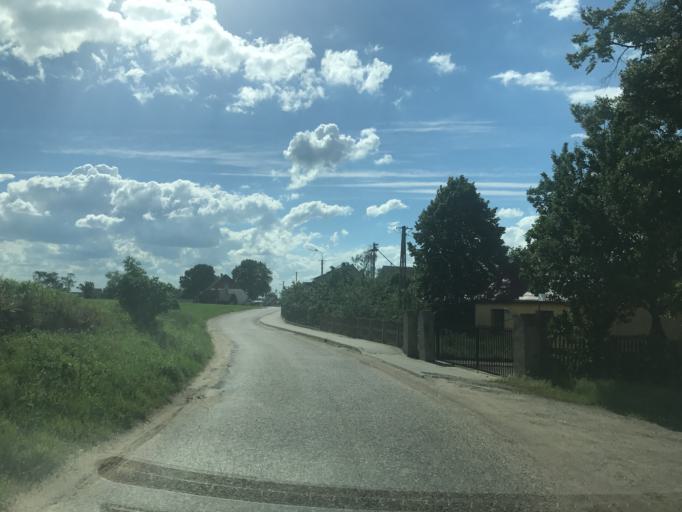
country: PL
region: Kujawsko-Pomorskie
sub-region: Powiat brodnicki
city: Brzozie
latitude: 53.3560
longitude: 19.6100
